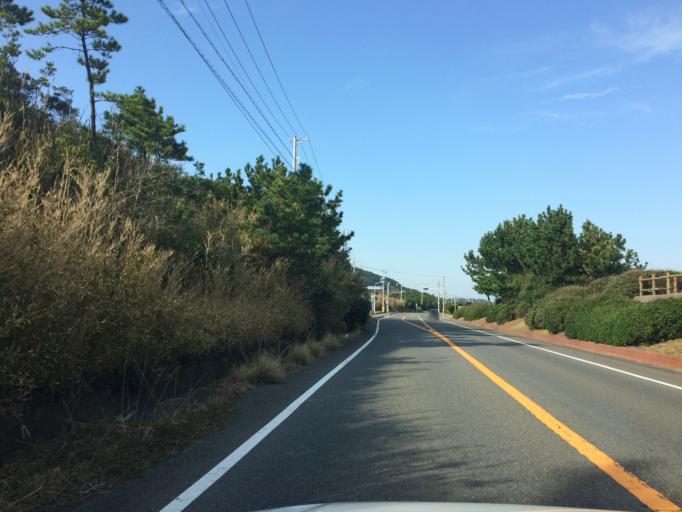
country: JP
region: Shizuoka
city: Oyama
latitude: 34.6410
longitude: 138.1934
